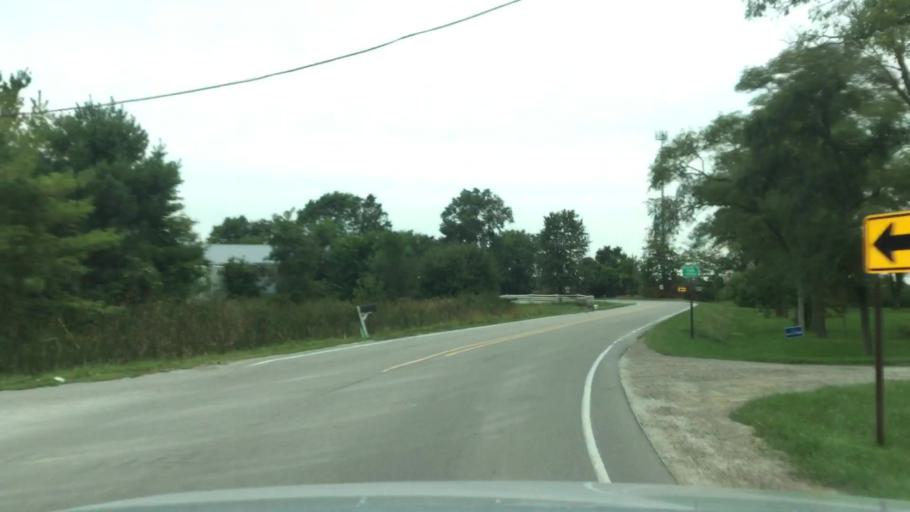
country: US
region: Michigan
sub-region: Washtenaw County
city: Milan
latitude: 42.0831
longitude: -83.7358
